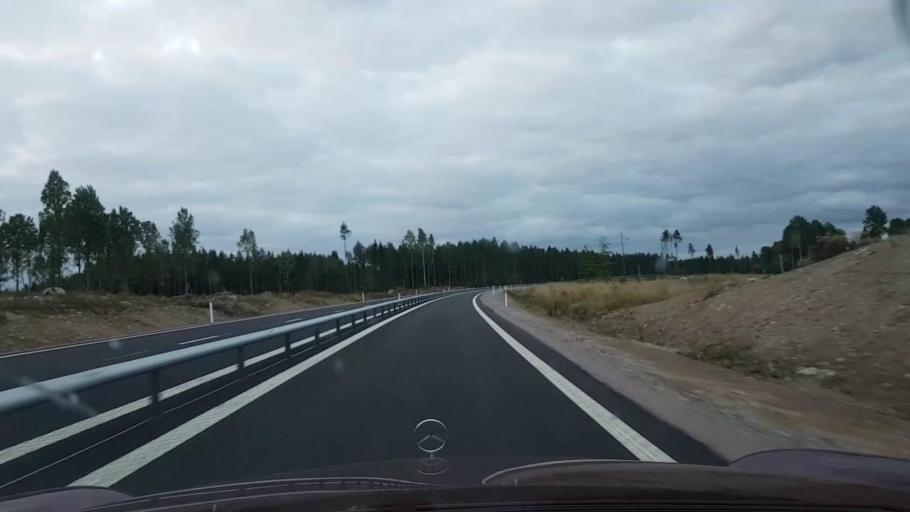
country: SE
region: Vaestmanland
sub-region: Hallstahammars Kommun
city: Hallstahammar
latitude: 59.6532
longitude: 16.2043
